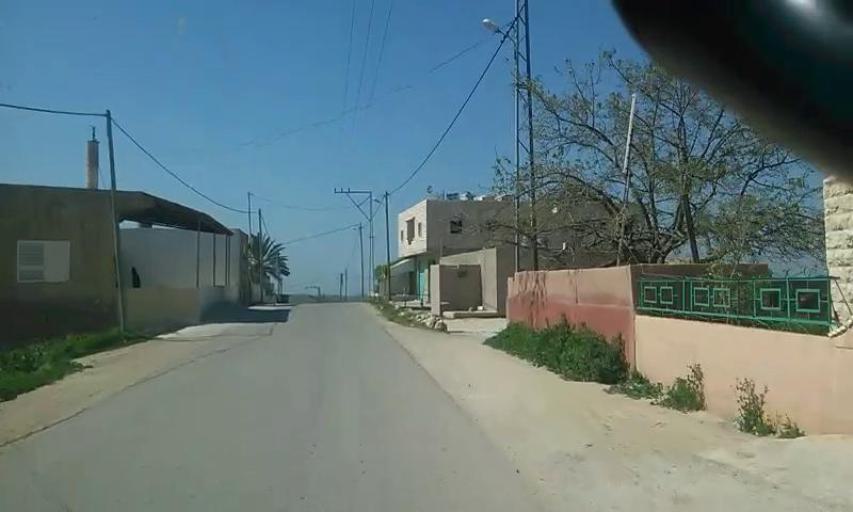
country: PS
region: West Bank
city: Al Majd
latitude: 31.4827
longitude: 34.9485
